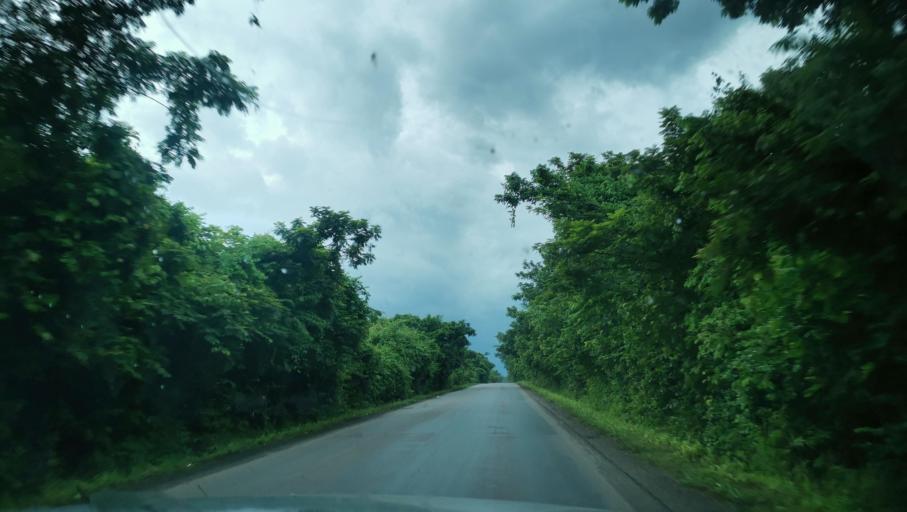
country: TH
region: Nakhon Phanom
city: Ban Phaeng
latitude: 17.8604
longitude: 104.4259
